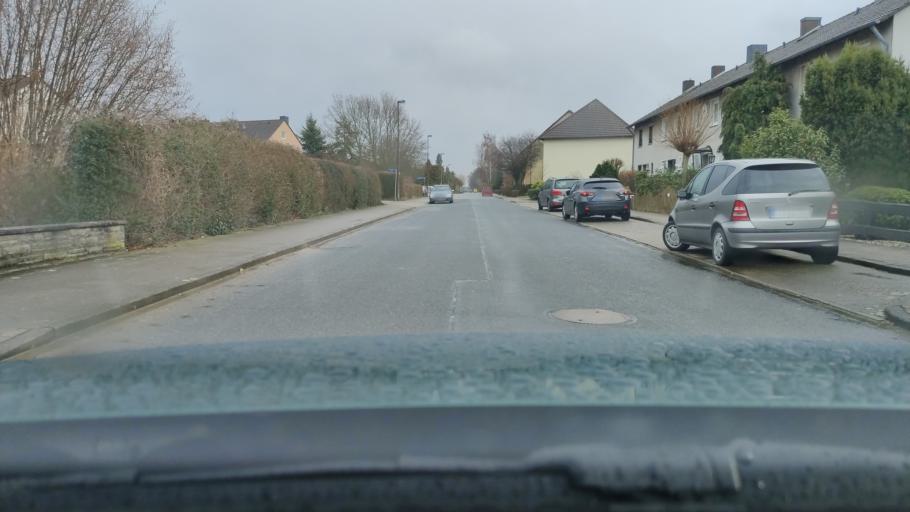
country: DE
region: Lower Saxony
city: Ilsede
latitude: 52.2706
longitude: 10.2268
